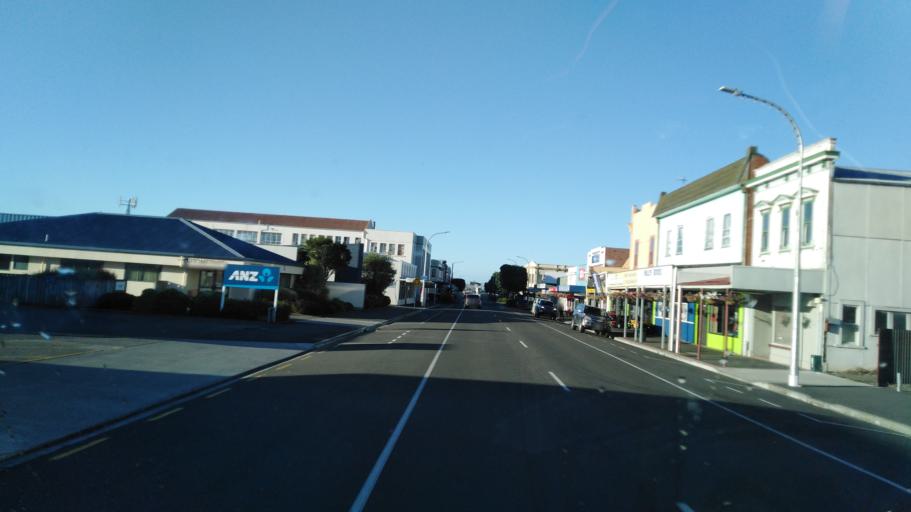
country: NZ
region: Manawatu-Wanganui
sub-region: Rangitikei District
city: Bulls
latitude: -40.0662
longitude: 175.3791
